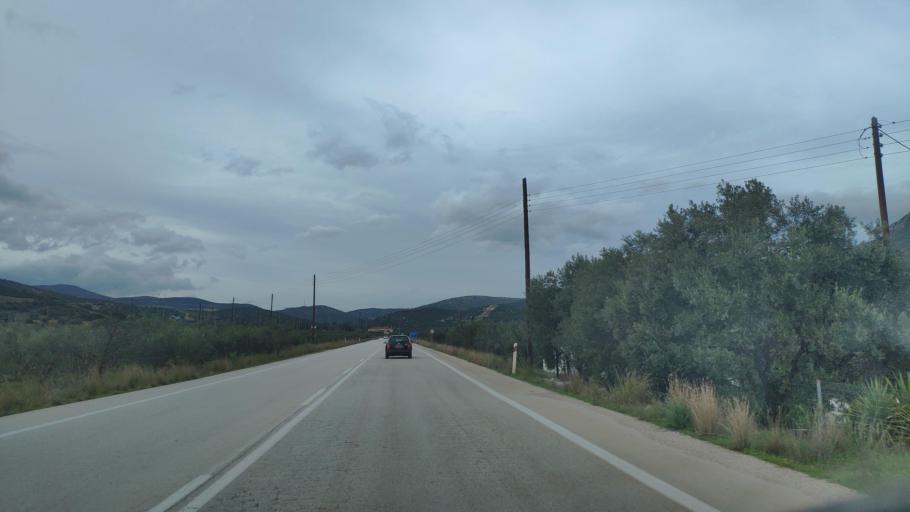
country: GR
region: Peloponnese
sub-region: Nomos Argolidos
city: Koutsopodi
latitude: 37.7498
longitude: 22.7356
